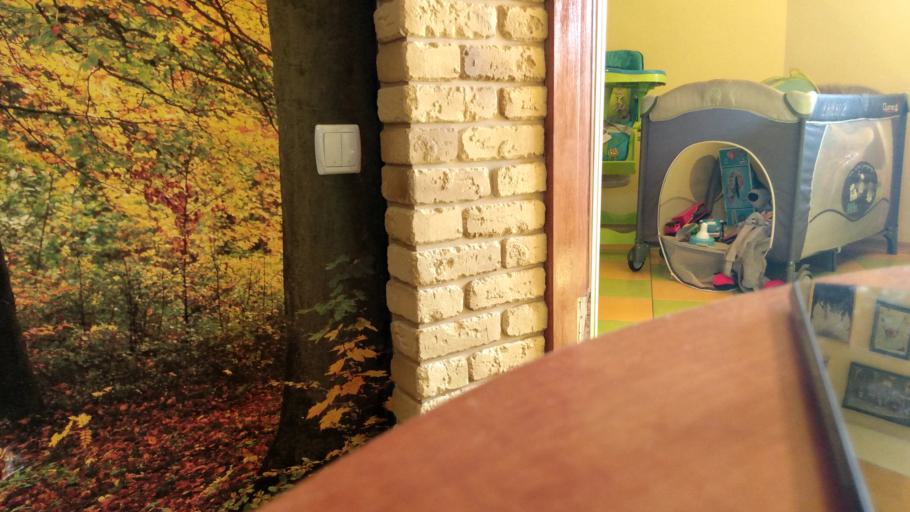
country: RU
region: Tverskaya
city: Vasil'yevskiy Mokh
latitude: 56.9699
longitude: 35.9336
